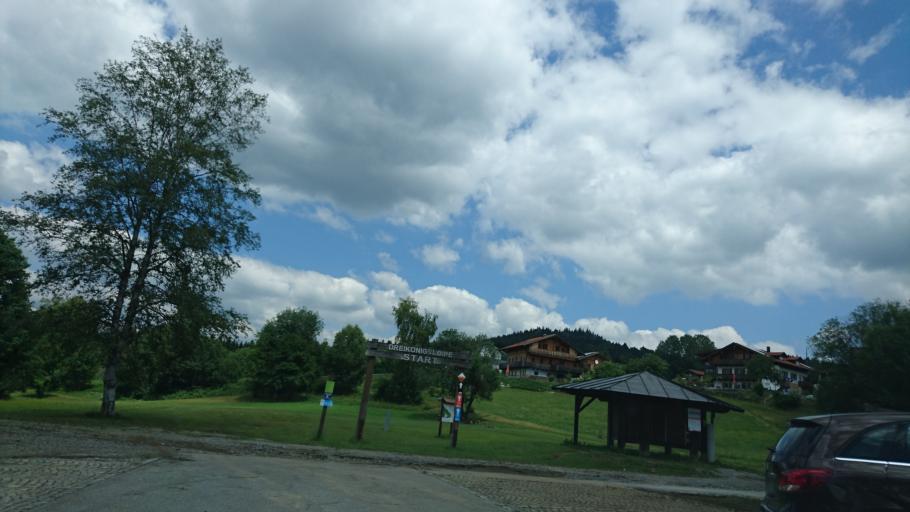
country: DE
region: Bavaria
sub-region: Lower Bavaria
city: Mauth
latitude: 48.8868
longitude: 13.5780
